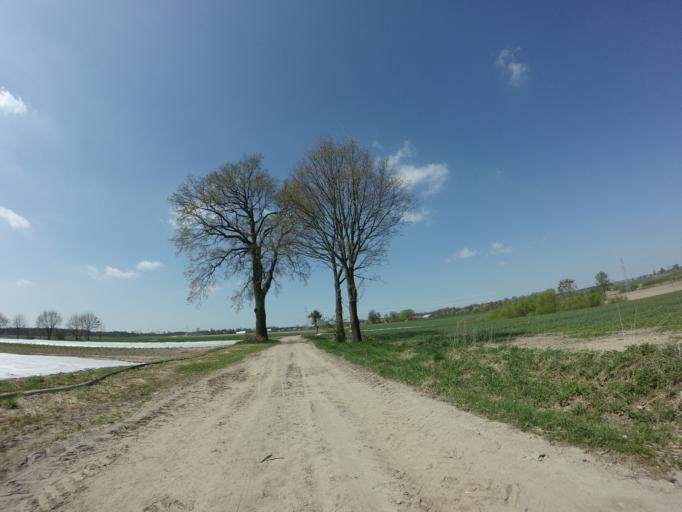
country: PL
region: West Pomeranian Voivodeship
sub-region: Powiat stargardzki
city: Suchan
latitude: 53.2240
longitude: 15.3133
